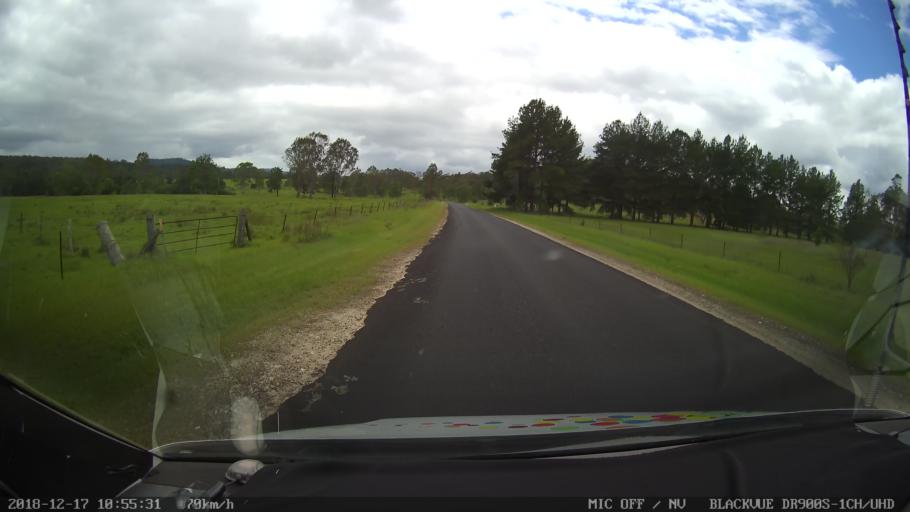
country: AU
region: New South Wales
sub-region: Richmond Valley
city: Casino
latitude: -28.8273
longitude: 152.5801
